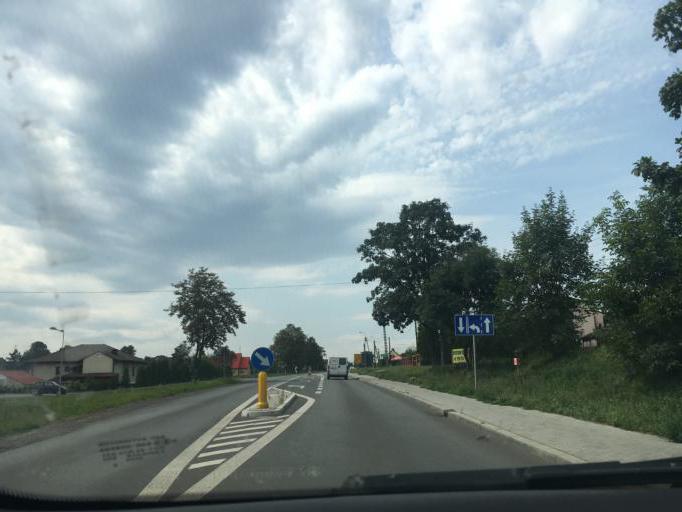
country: PL
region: Silesian Voivodeship
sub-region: Powiat raciborski
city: Kornowac
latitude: 50.0694
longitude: 18.3431
